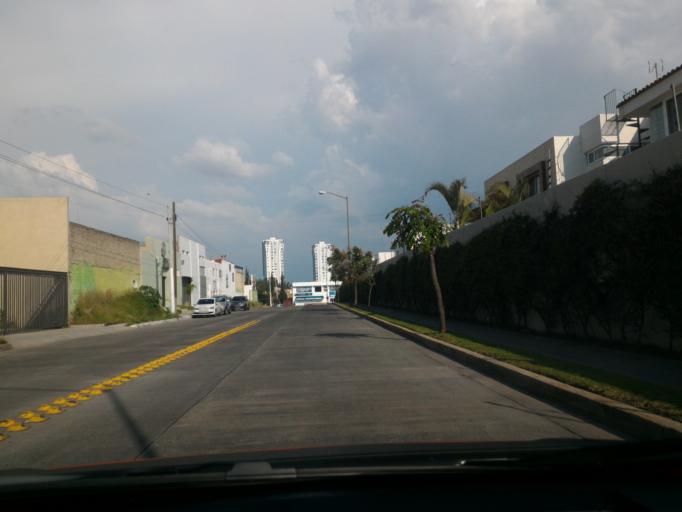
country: MX
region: Jalisco
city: Guadalajara
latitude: 20.6640
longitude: -103.4385
